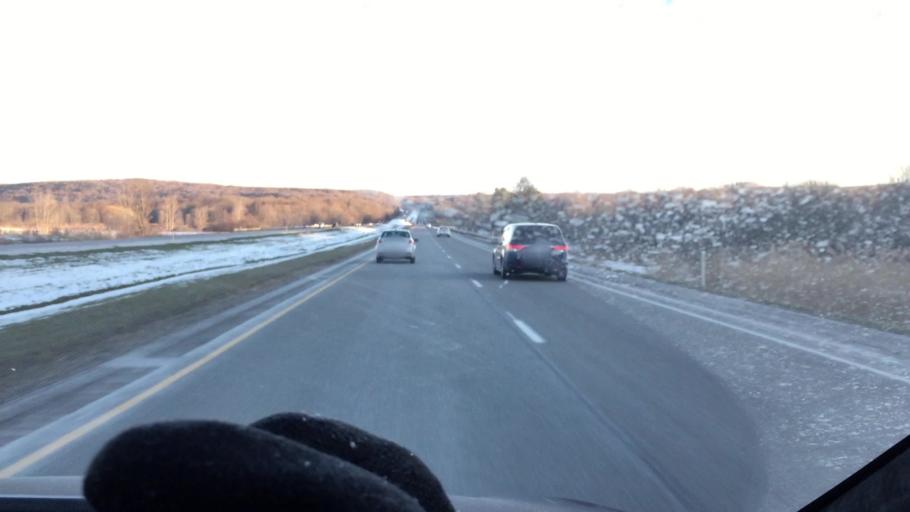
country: US
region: Pennsylvania
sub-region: Crawford County
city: Meadville
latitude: 41.6689
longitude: -80.2088
